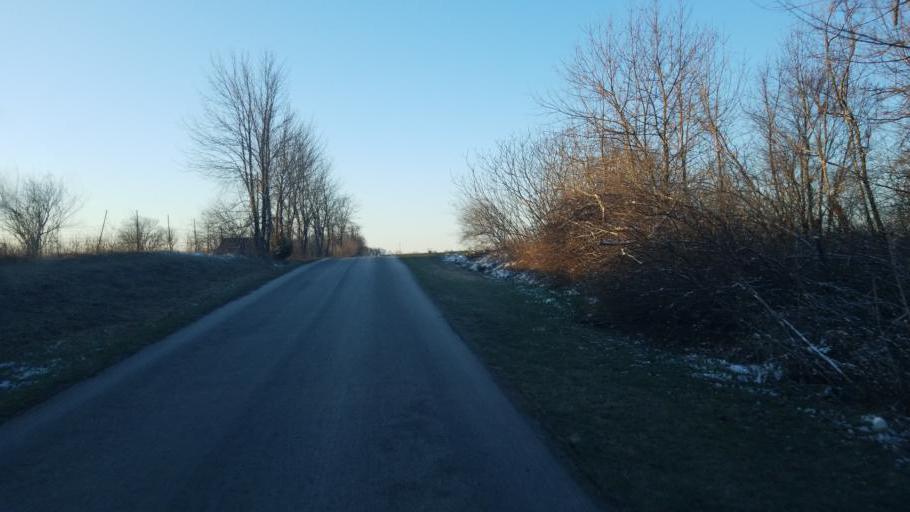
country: US
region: Ohio
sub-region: Highland County
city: Leesburg
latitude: 39.2770
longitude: -83.5018
